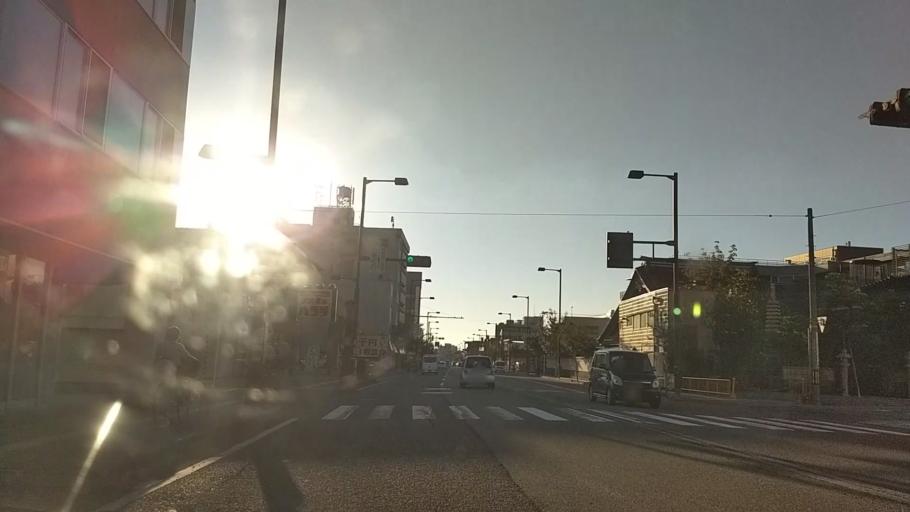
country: JP
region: Ishikawa
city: Nonoichi
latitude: 36.5580
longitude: 136.6459
